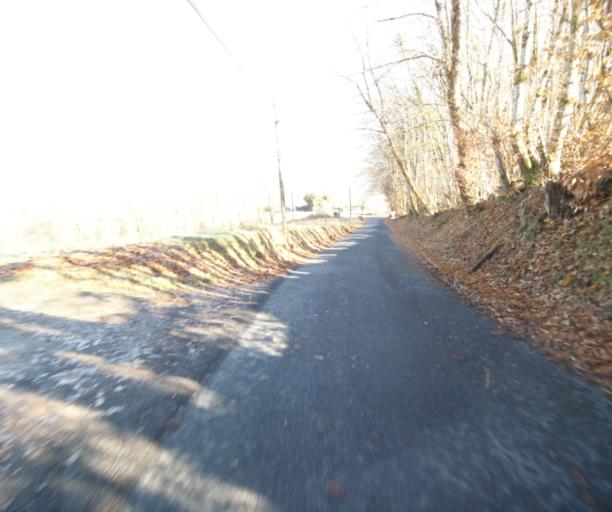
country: FR
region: Limousin
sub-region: Departement de la Correze
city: Laguenne
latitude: 45.2430
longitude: 1.7562
